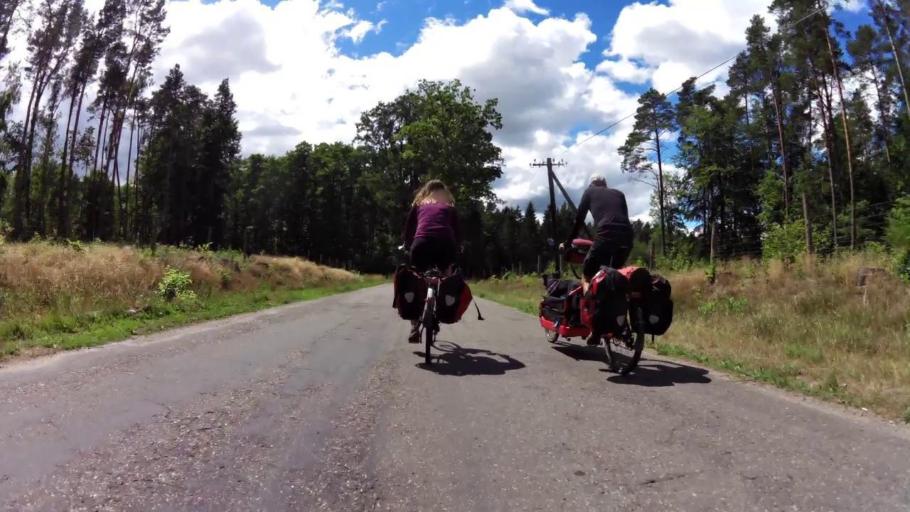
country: PL
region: West Pomeranian Voivodeship
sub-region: Powiat lobeski
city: Resko
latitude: 53.7529
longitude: 15.5064
